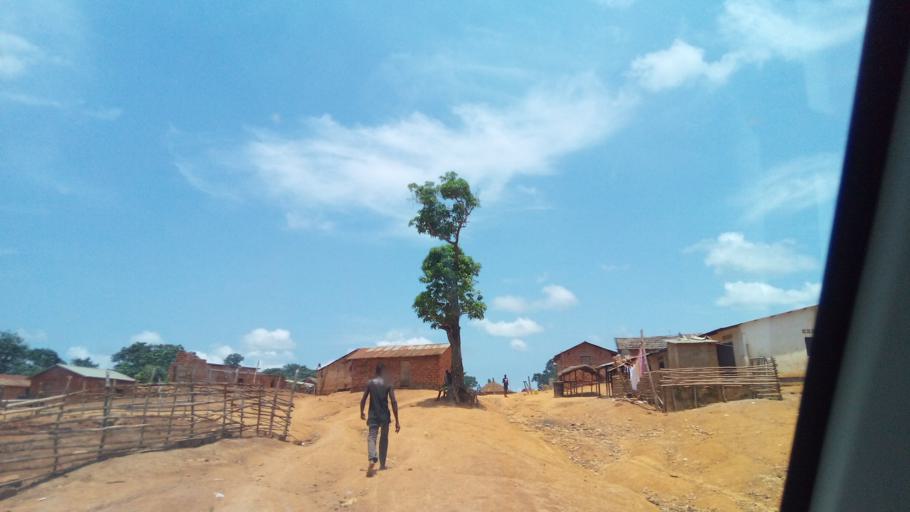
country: AO
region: Zaire
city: Mbanza Congo
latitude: -5.8140
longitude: 14.2455
